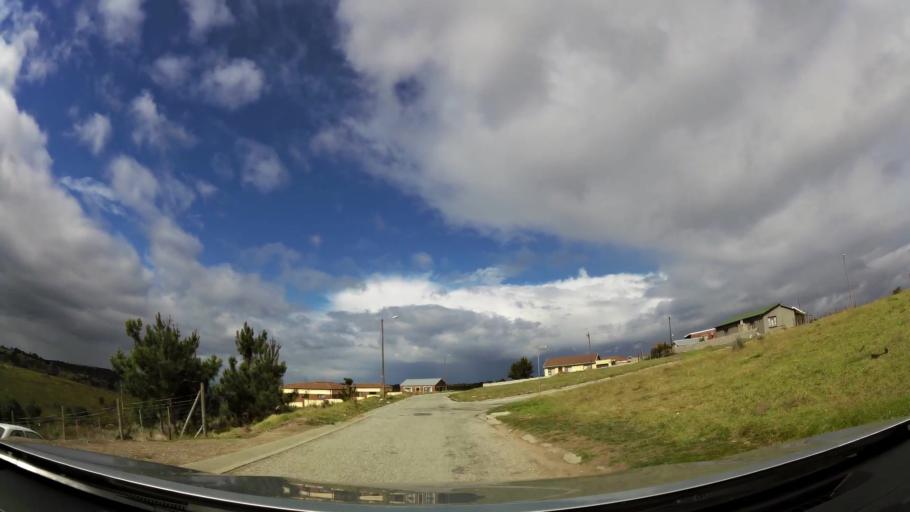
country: ZA
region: Western Cape
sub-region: Eden District Municipality
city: George
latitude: -34.0257
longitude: 22.4765
